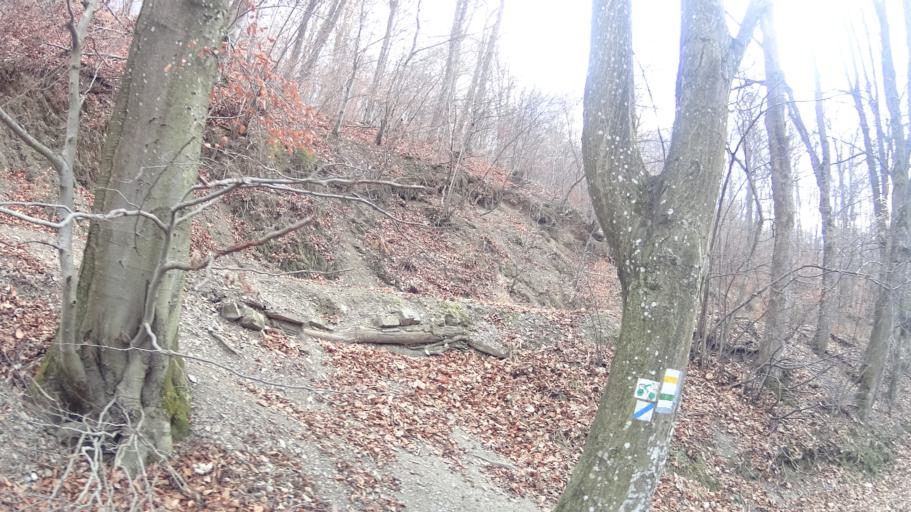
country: HU
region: Heves
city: Szilvasvarad
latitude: 48.0839
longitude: 20.4069
